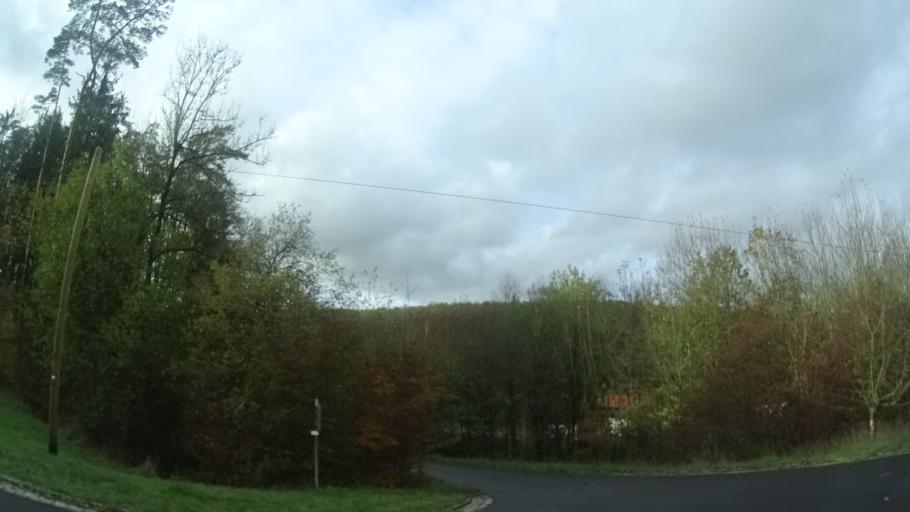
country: DE
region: Bavaria
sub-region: Regierungsbezirk Unterfranken
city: Aubstadt
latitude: 50.3444
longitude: 10.4131
